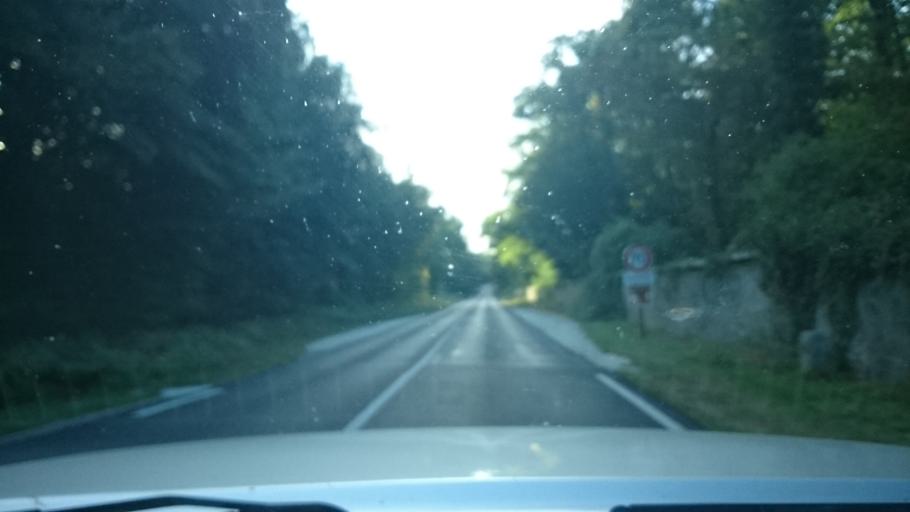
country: FR
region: Ile-de-France
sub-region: Departement de Seine-et-Marne
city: Samoreau
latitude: 48.4054
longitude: 2.7521
